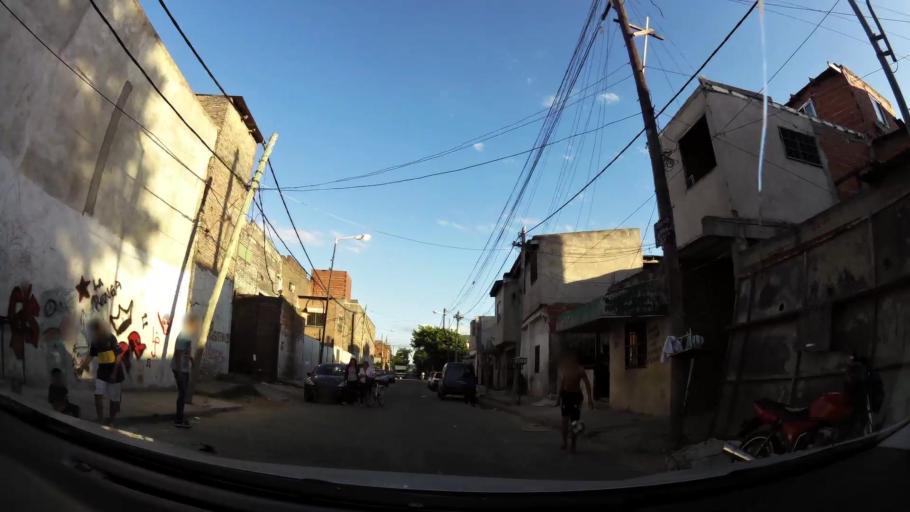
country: AR
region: Buenos Aires
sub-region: Partido de Tigre
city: Tigre
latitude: -34.4438
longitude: -58.5754
